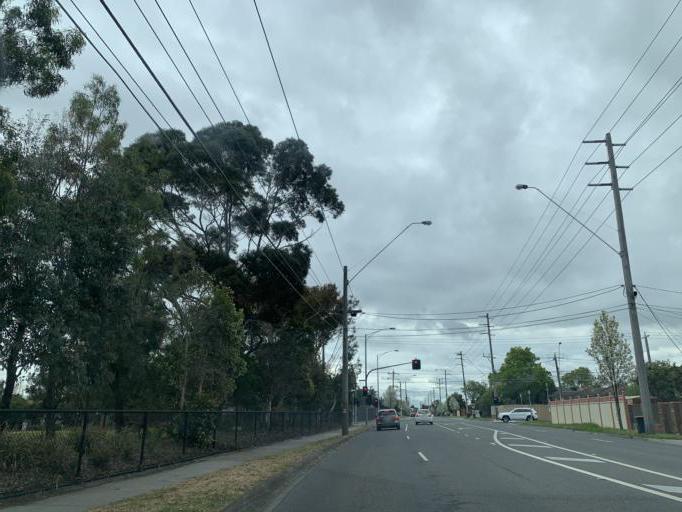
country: AU
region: Victoria
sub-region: Kingston
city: Mentone
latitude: -37.9755
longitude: 145.0726
